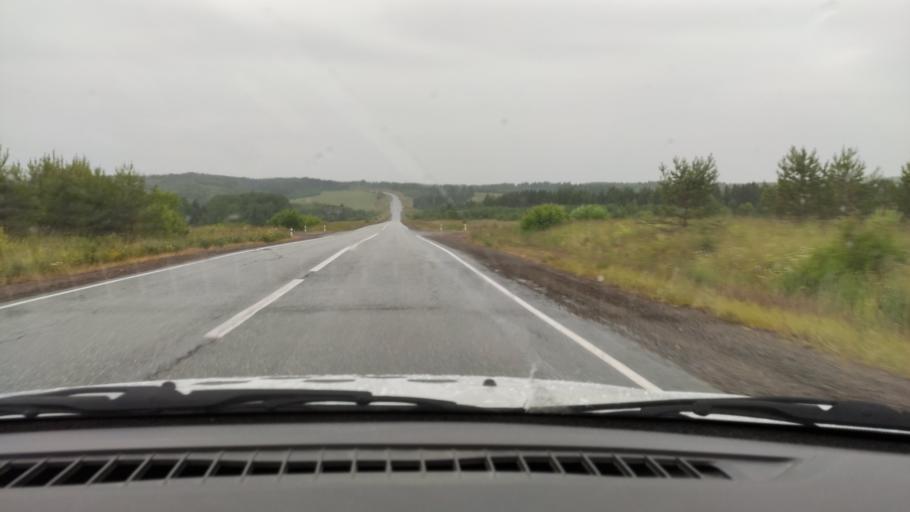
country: RU
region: Udmurtiya
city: Votkinsk
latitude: 57.2660
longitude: 54.2522
